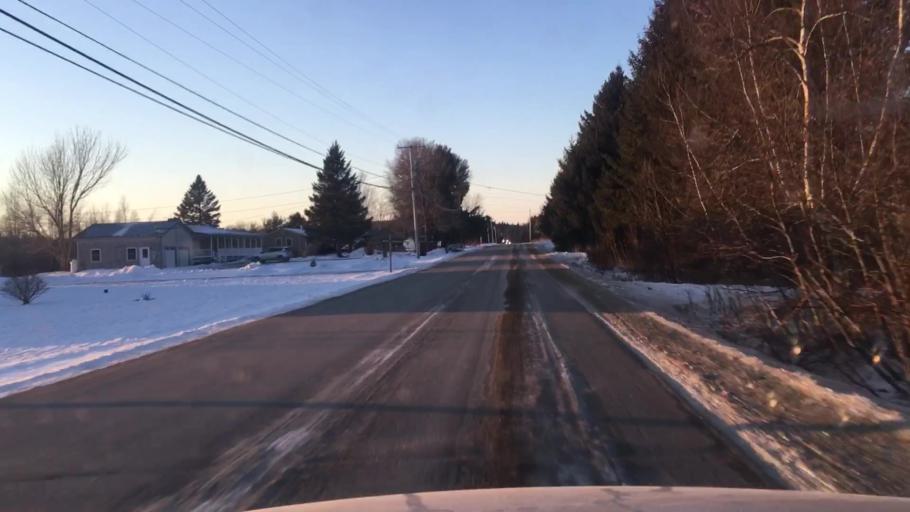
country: US
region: Maine
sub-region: Penobscot County
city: Brewer
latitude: 44.7317
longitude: -68.7599
